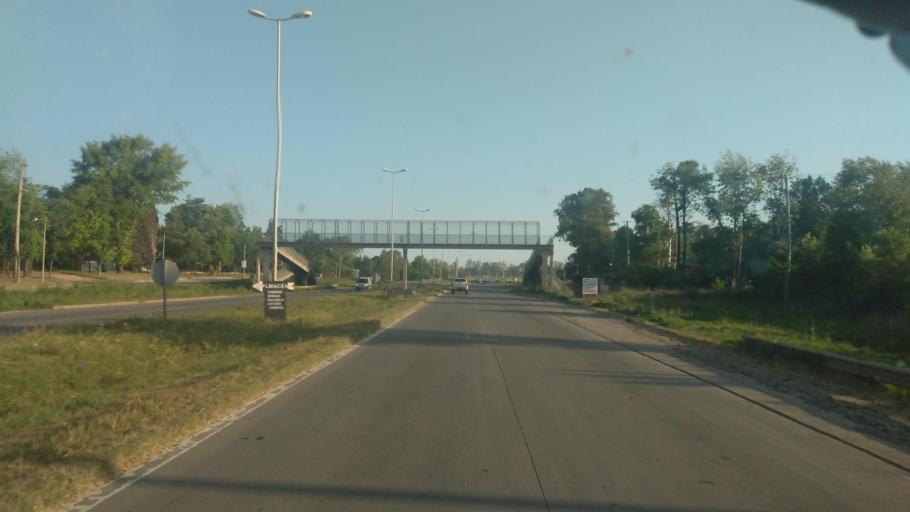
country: AR
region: Buenos Aires
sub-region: Partido de Campana
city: Campana
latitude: -34.2496
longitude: -58.9652
